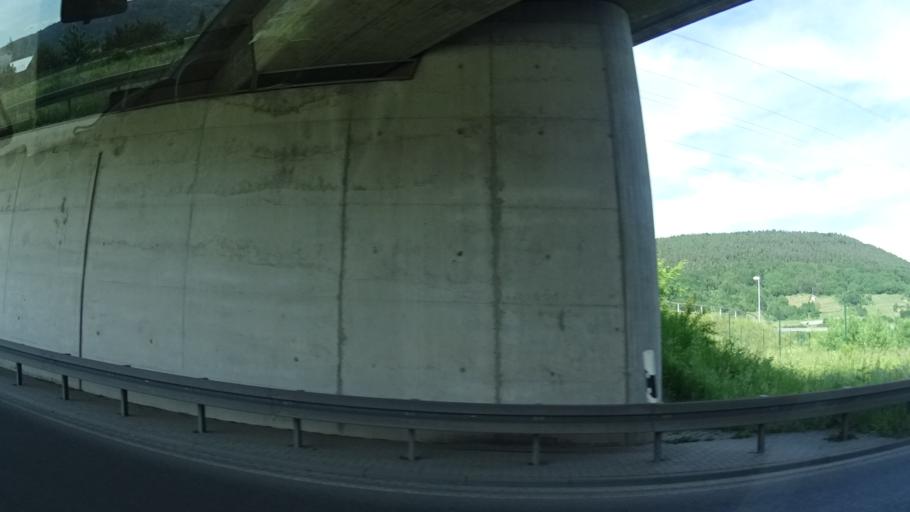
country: DE
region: Bavaria
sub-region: Regierungsbezirk Unterfranken
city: Grossheubach
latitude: 49.7152
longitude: 9.2374
